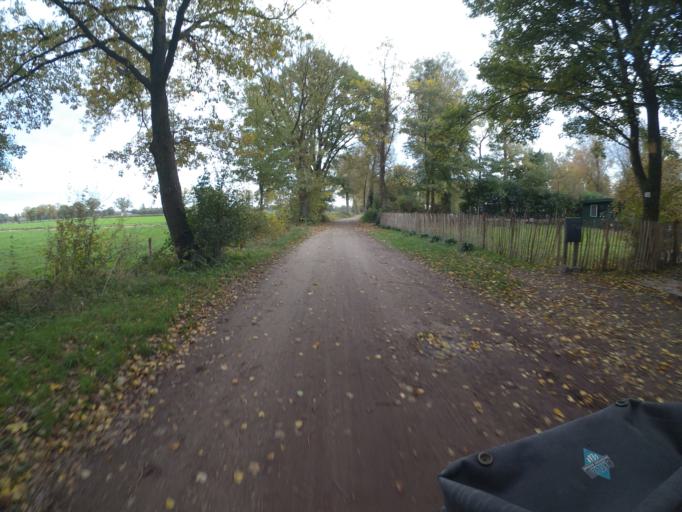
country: NL
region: North Brabant
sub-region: Gemeente Haaren
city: Haaren
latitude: 51.6159
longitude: 5.2599
